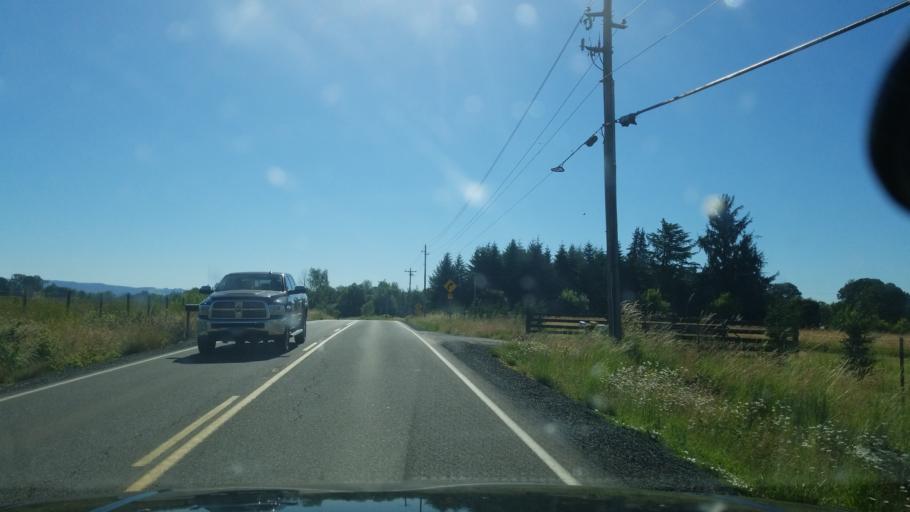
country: US
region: Oregon
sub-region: Yamhill County
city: McMinnville
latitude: 45.2305
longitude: -123.2354
